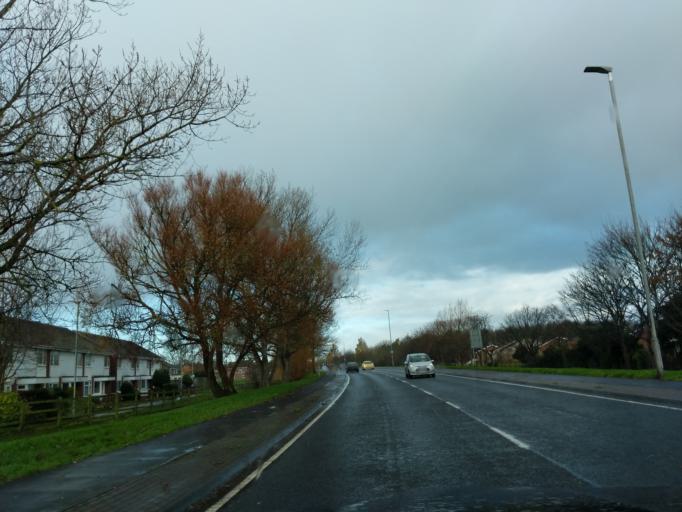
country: GB
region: England
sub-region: Northumberland
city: Blyth
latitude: 55.1160
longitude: -1.5077
